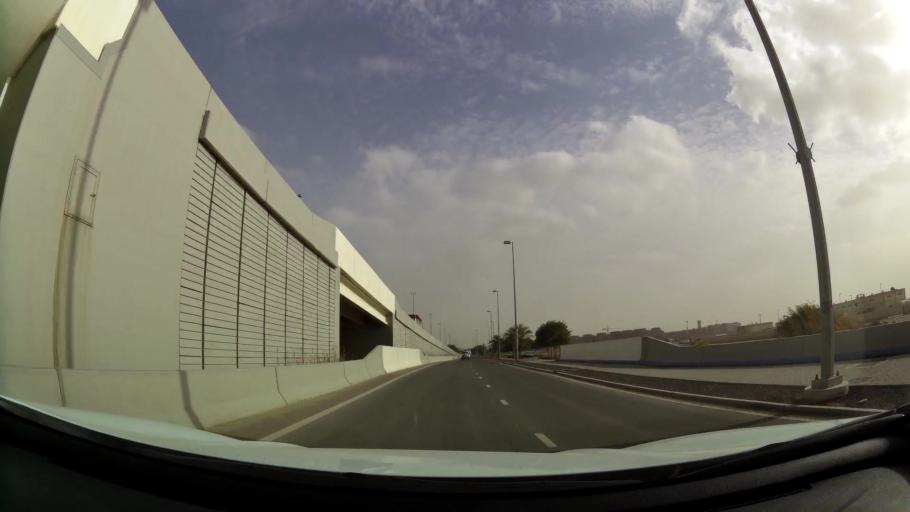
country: AE
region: Abu Dhabi
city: Abu Dhabi
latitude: 24.4456
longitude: 54.6187
